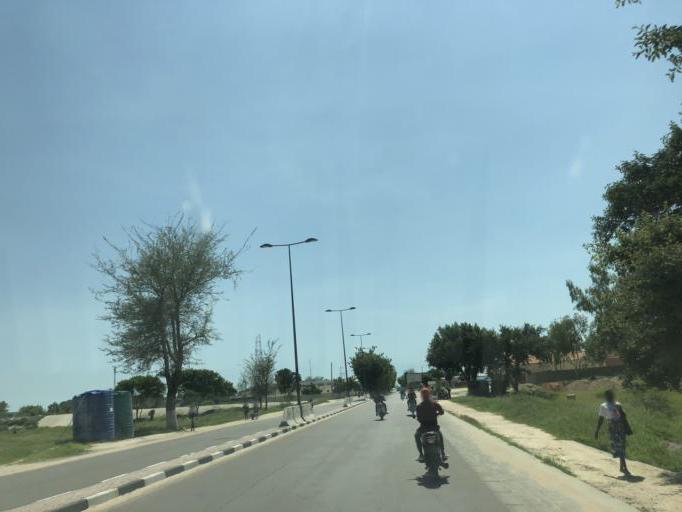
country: AO
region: Cunene
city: Ondjiva
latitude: -17.0692
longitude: 15.7192
